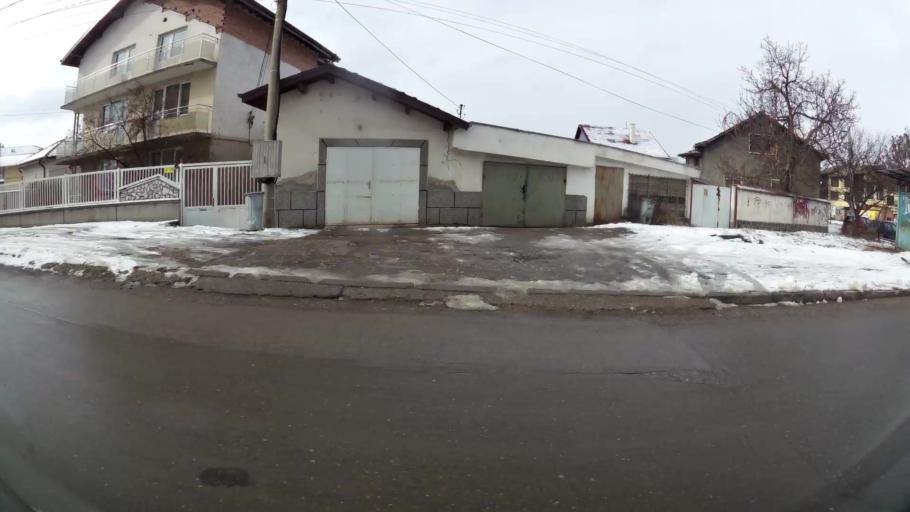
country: BG
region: Sofia-Capital
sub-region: Stolichna Obshtina
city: Sofia
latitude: 42.7124
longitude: 23.4200
